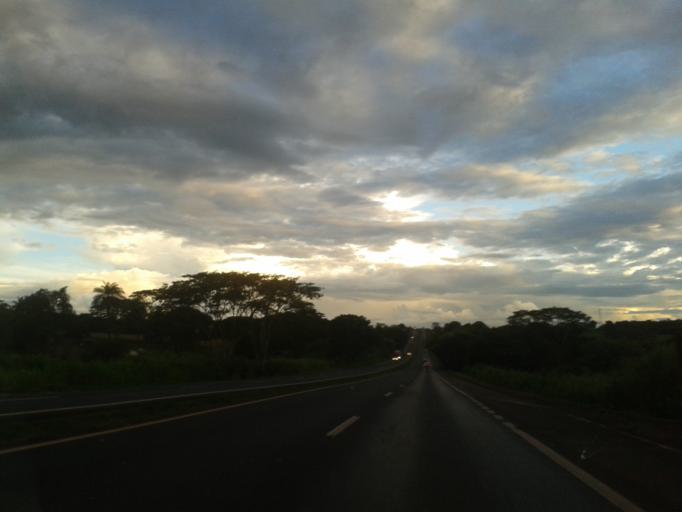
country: BR
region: Minas Gerais
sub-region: Centralina
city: Centralina
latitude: -18.6572
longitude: -49.1689
